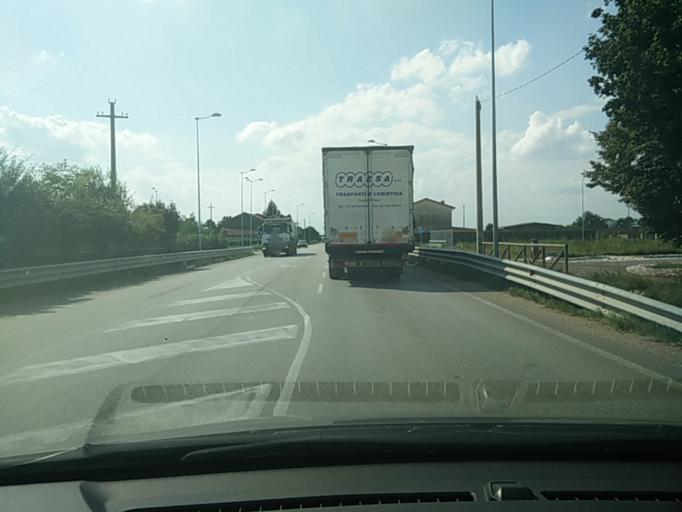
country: IT
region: Veneto
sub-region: Provincia di Treviso
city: Musano
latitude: 45.7149
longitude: 12.1140
